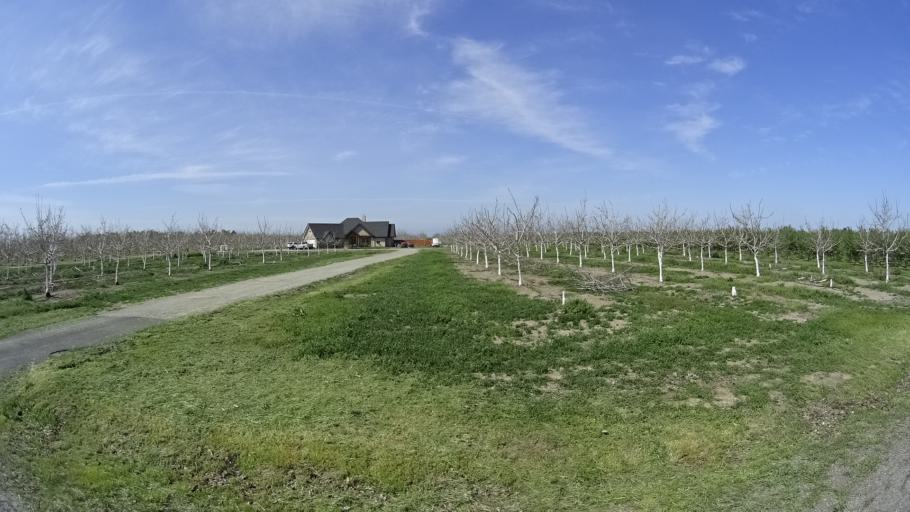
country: US
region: California
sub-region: Glenn County
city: Hamilton City
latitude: 39.8011
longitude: -122.0852
